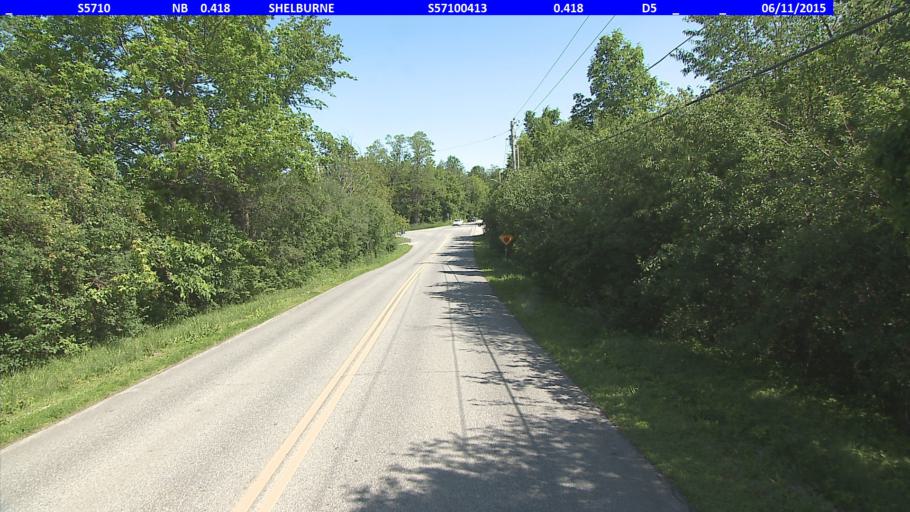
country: US
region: Vermont
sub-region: Chittenden County
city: Hinesburg
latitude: 44.3706
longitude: -73.1810
